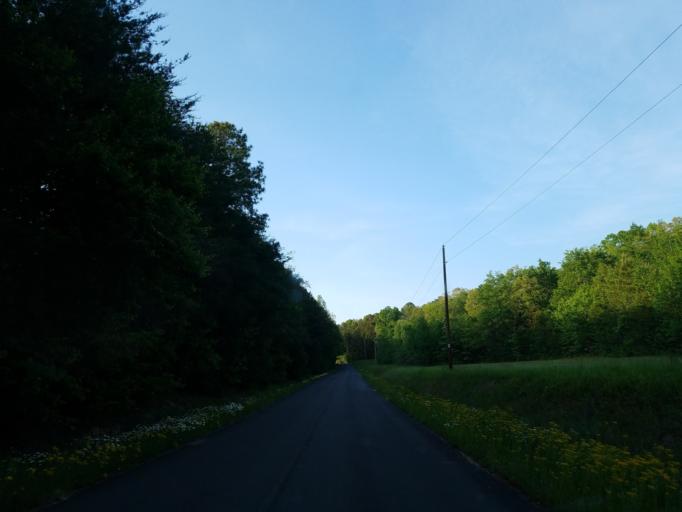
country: US
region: Georgia
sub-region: Whitfield County
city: Dalton
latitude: 34.6520
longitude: -85.0831
